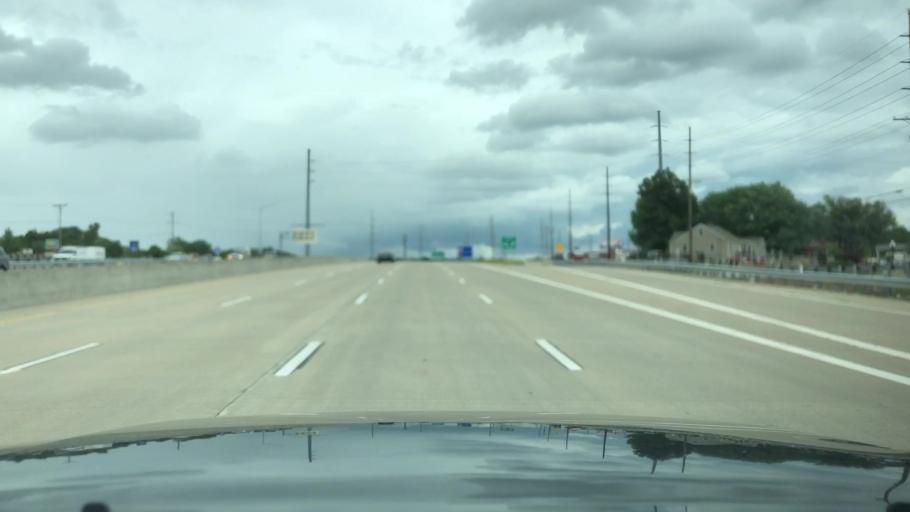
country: US
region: Missouri
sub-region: Saint Charles County
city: Cottleville
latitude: 38.7437
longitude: -90.6048
